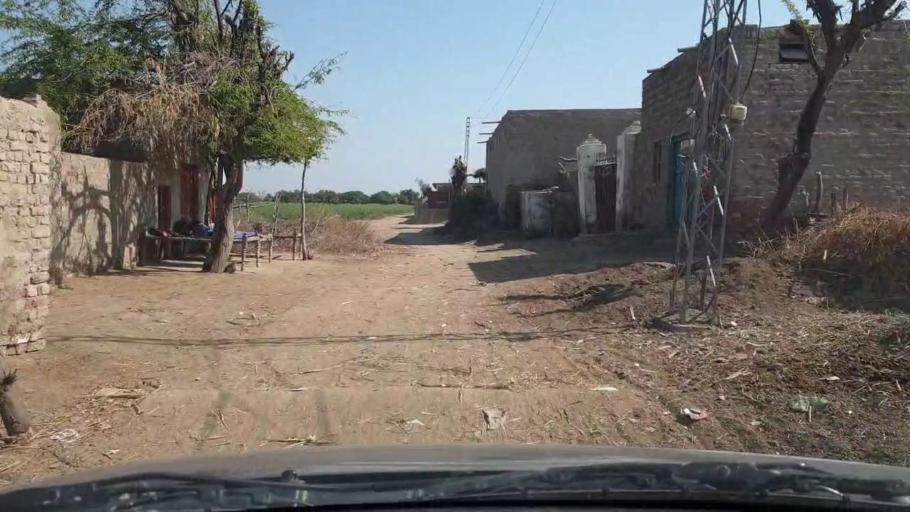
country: PK
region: Sindh
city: Samaro
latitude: 25.2437
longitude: 69.2472
